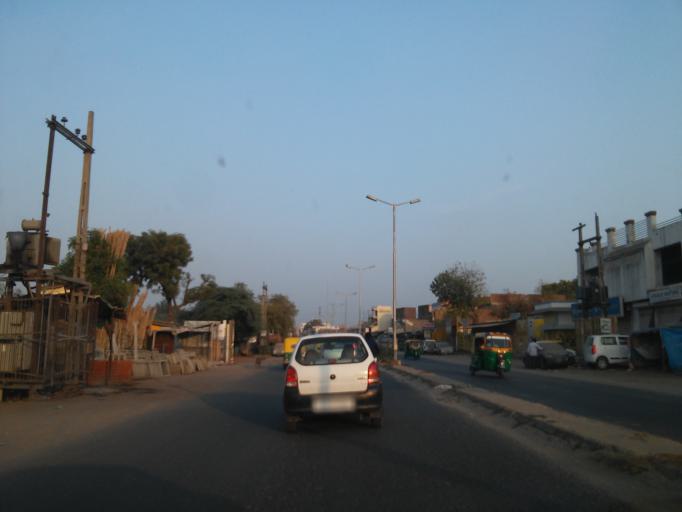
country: IN
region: Gujarat
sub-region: Ahmadabad
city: Sarkhej
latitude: 22.9871
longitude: 72.4995
